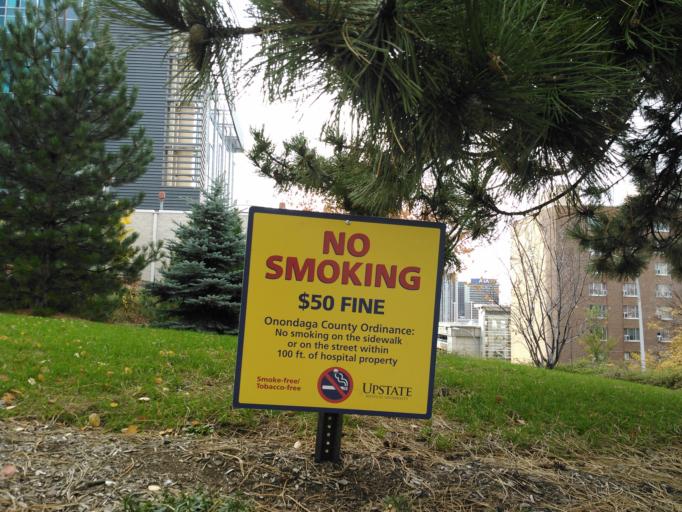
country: US
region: New York
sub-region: Onondaga County
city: Syracuse
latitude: 43.0426
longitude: -76.1380
